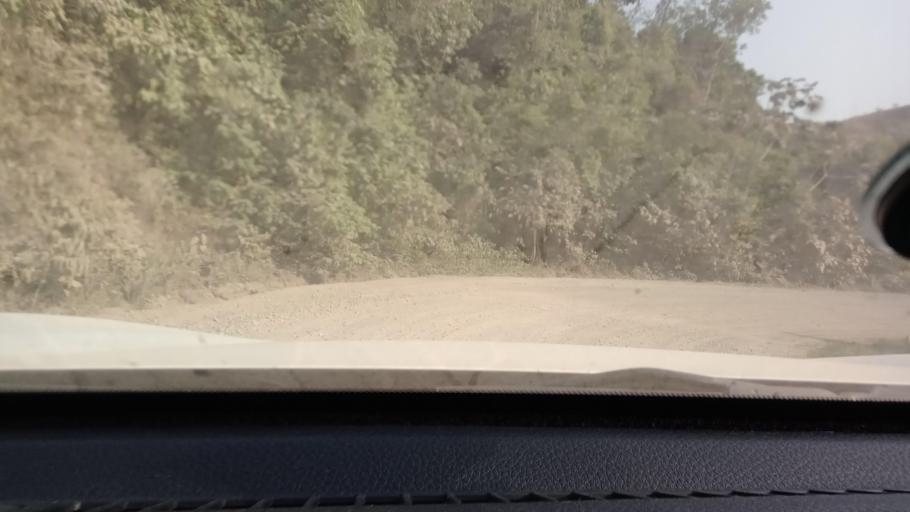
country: MX
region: Tabasco
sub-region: Huimanguillo
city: Francisco Rueda
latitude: 17.6641
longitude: -93.8653
